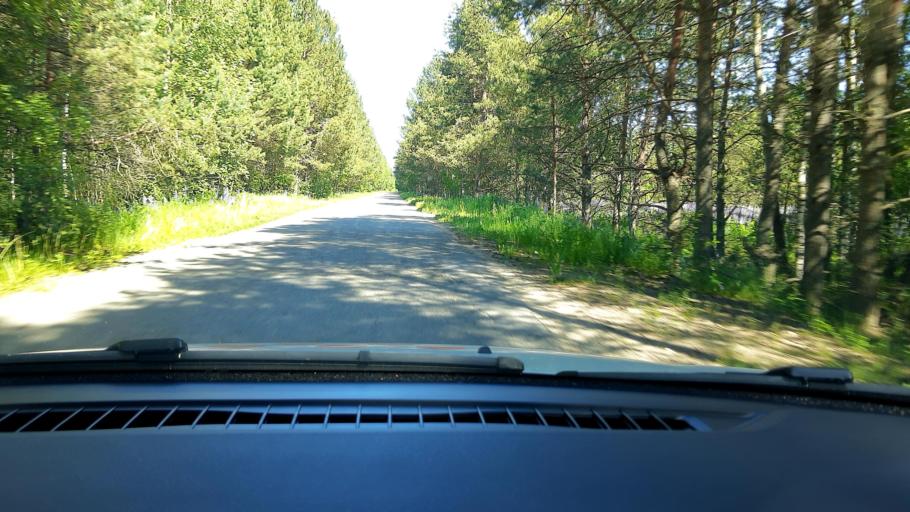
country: RU
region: Nizjnij Novgorod
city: Sitniki
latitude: 56.5234
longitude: 44.1479
